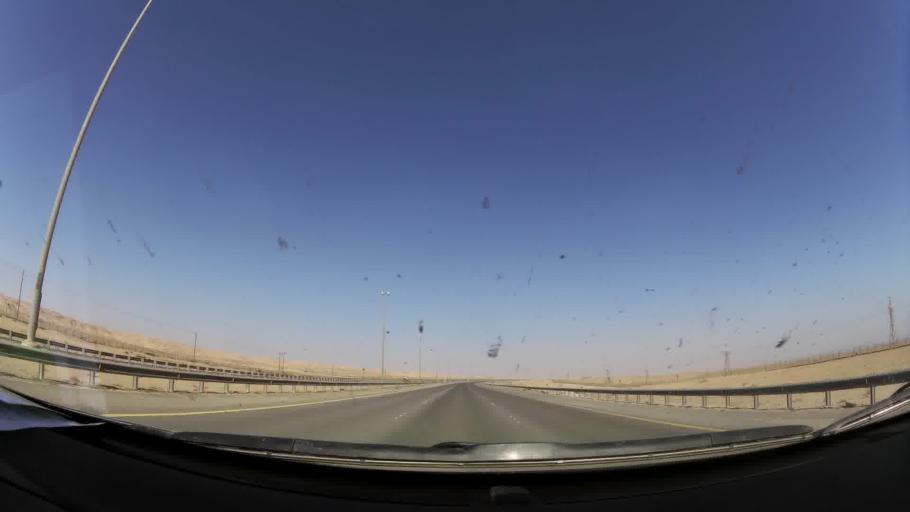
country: KW
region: Muhafazat al Jahra'
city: Al Jahra'
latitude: 29.5113
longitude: 47.8023
